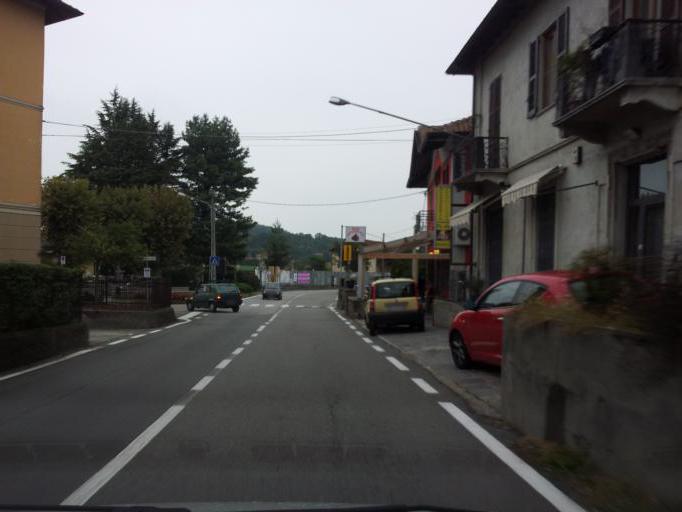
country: IT
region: Lombardy
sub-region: Provincia di Varese
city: Ternate
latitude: 45.7816
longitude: 8.7015
